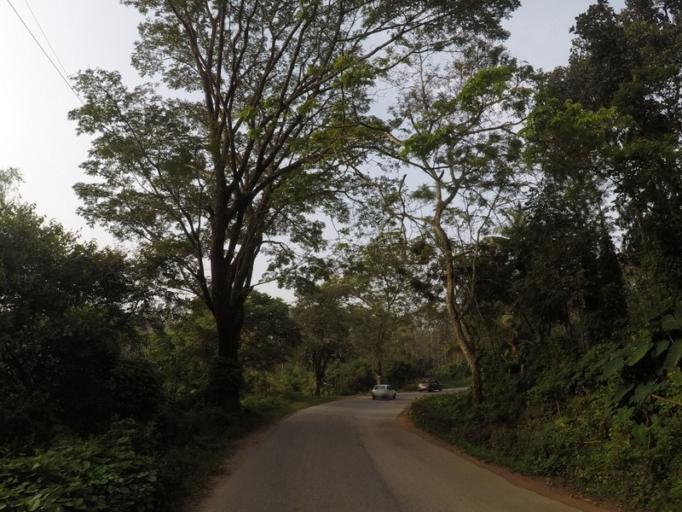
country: IN
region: Karnataka
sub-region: Chikmagalur
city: Chikmagalur
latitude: 13.2603
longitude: 75.6801
